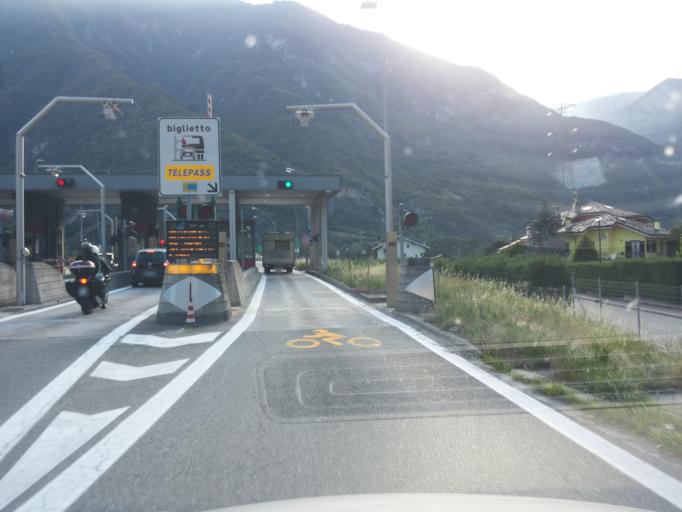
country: IT
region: Aosta Valley
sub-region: Valle d'Aosta
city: Verres
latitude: 45.6694
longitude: 7.6863
